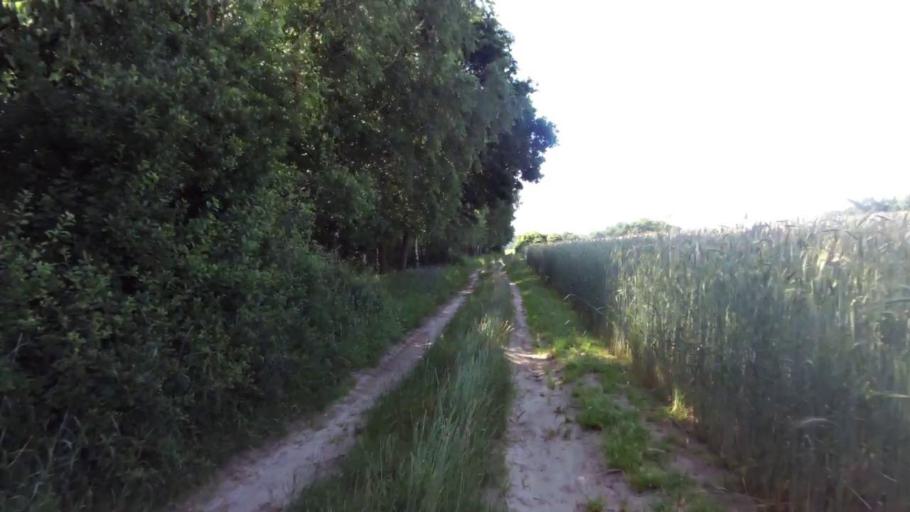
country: PL
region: West Pomeranian Voivodeship
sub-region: Powiat swidwinski
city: Polczyn-Zdroj
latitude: 53.8908
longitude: 16.0898
